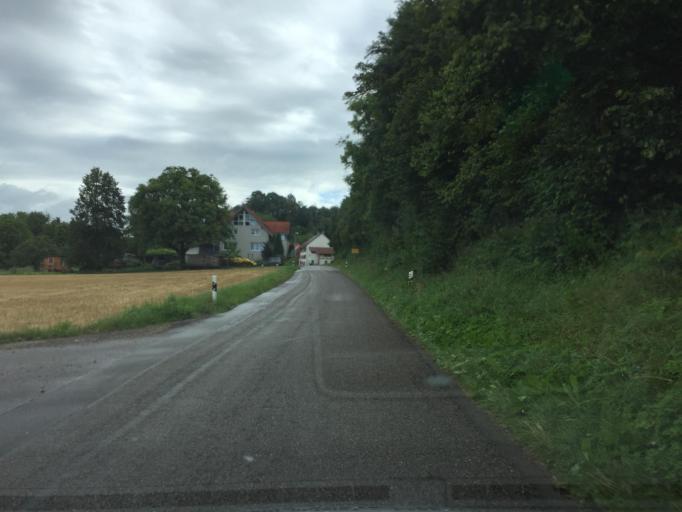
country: CH
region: Schaffhausen
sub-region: Bezirk Unterklettgau
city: Wilchingen
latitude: 47.6427
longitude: 8.4569
